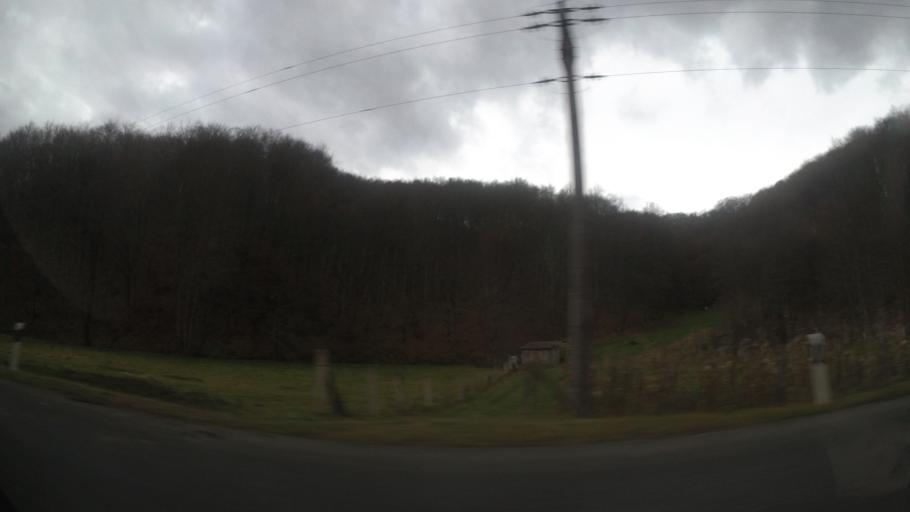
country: HR
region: Karlovacka
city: Vojnic
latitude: 45.3266
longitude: 15.6623
